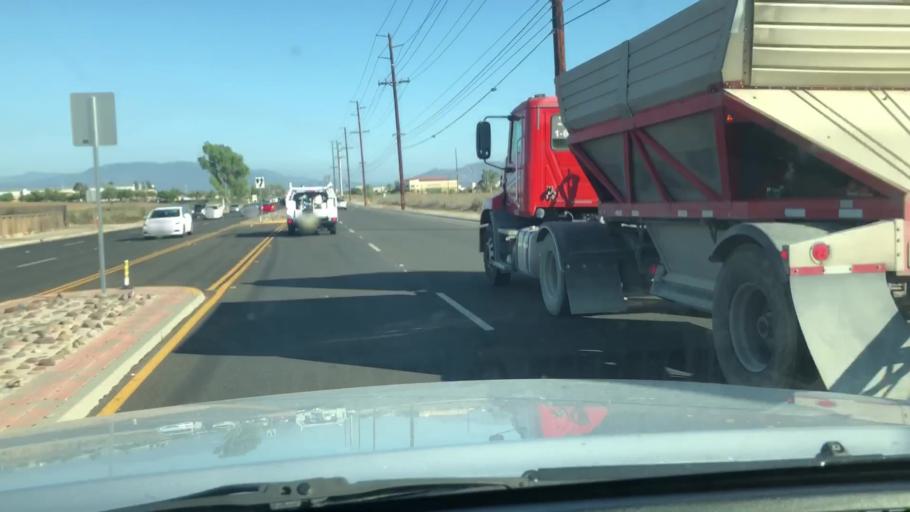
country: US
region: California
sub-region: Riverside County
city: Murrieta
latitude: 33.5481
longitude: -117.1963
